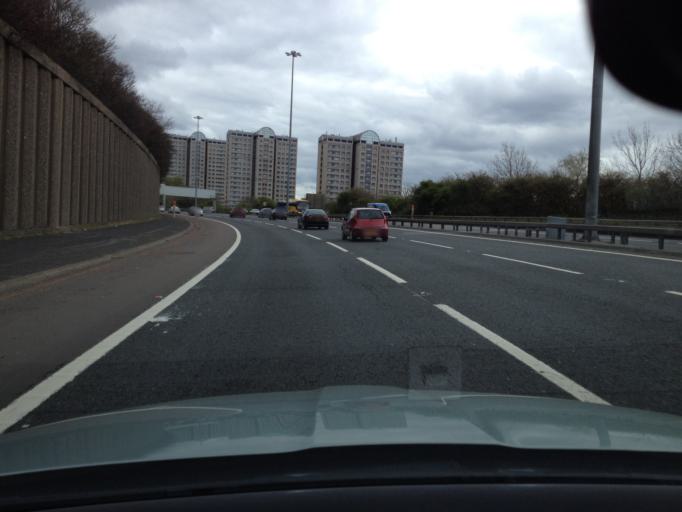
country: GB
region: Scotland
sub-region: North Lanarkshire
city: Stepps
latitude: 55.8680
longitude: -4.1717
